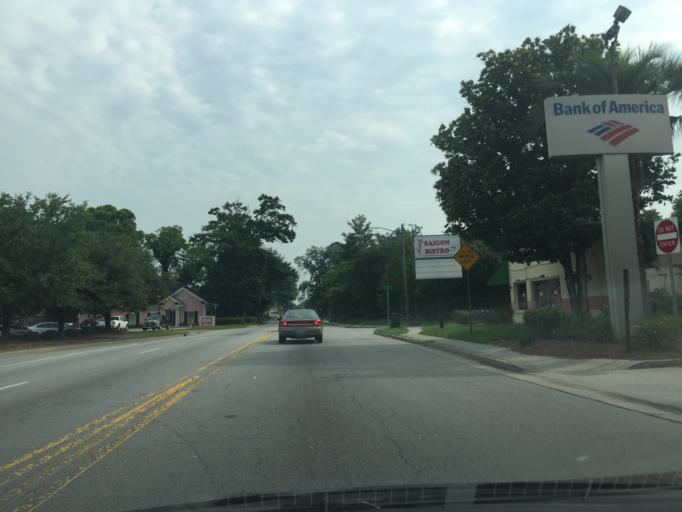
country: US
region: Georgia
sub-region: Chatham County
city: Thunderbolt
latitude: 32.0253
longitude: -81.0943
